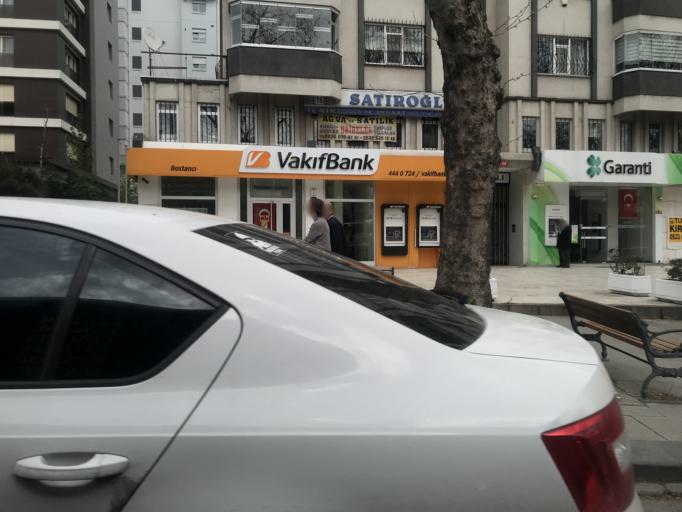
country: TR
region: Istanbul
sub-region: Atasehir
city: Atasehir
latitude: 40.9631
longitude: 29.0901
